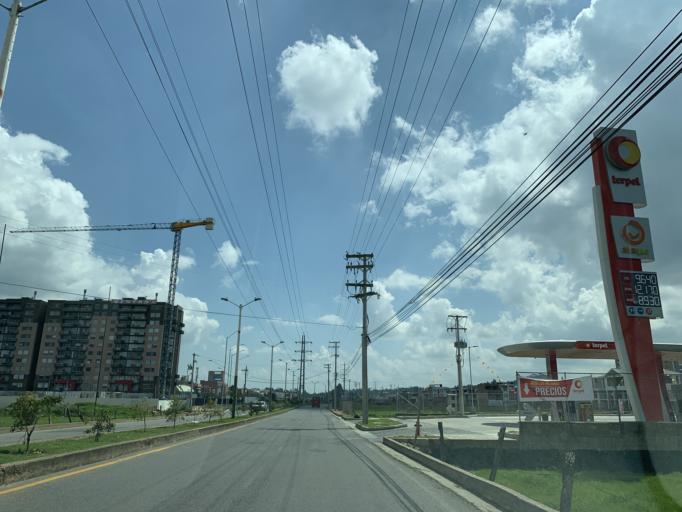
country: CO
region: Boyaca
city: Tunja
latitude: 5.5600
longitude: -73.3427
